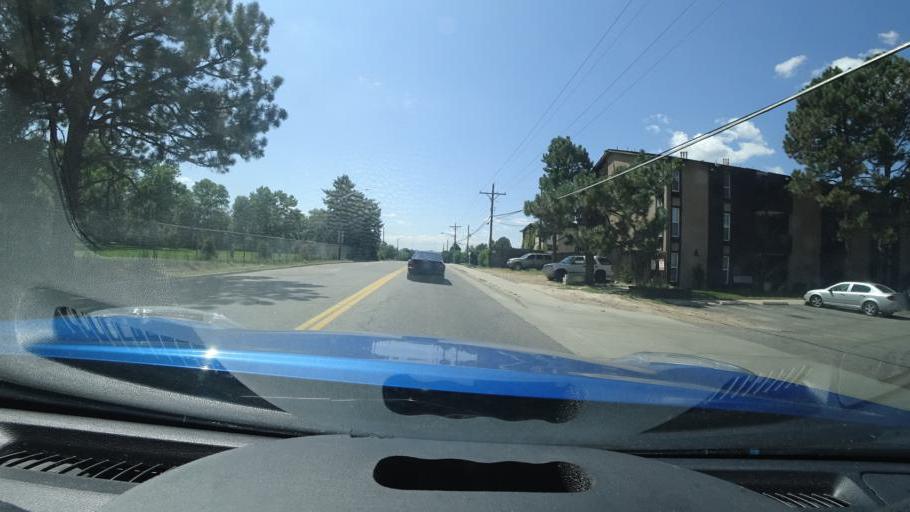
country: US
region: Colorado
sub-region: Arapahoe County
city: Glendale
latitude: 39.7012
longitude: -104.9035
